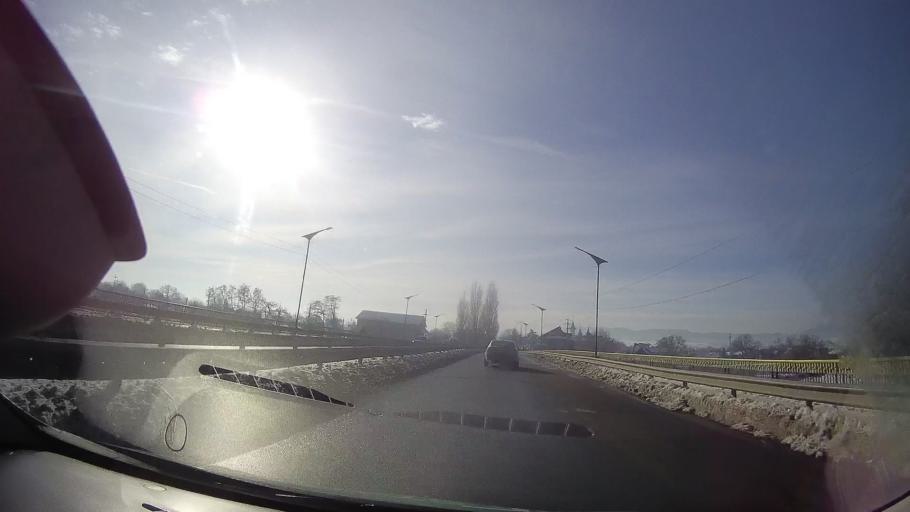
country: RO
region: Neamt
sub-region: Oras Targu Neamt
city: Humulesti
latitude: 47.2014
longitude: 26.3575
